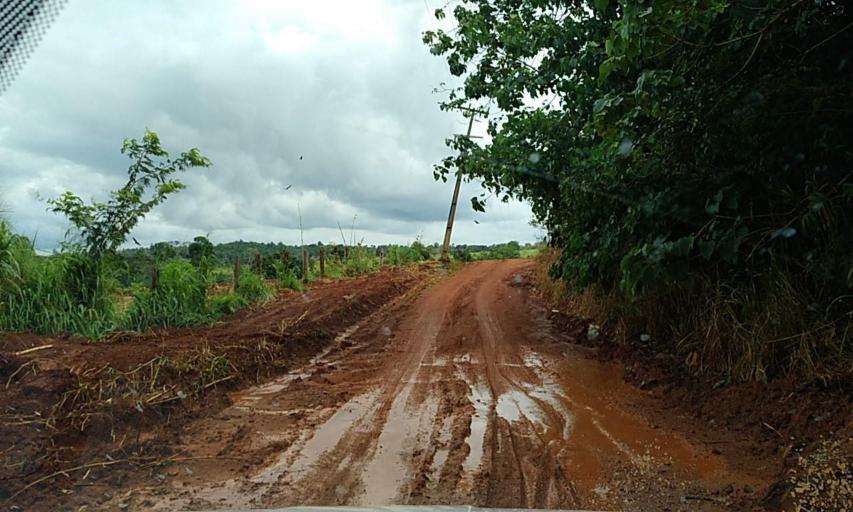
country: BR
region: Para
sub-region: Altamira
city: Altamira
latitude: -3.3176
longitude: -52.6849
